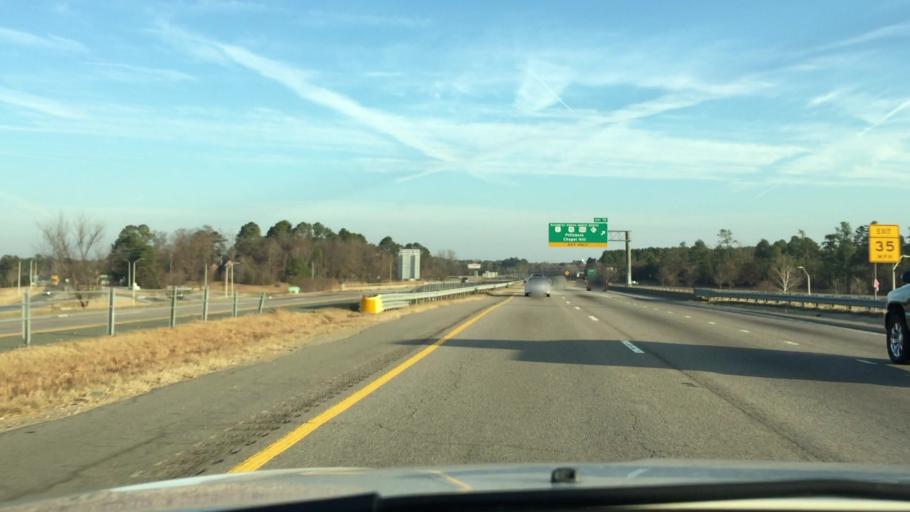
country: US
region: North Carolina
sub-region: Lee County
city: Sanford
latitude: 35.5225
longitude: -79.1841
